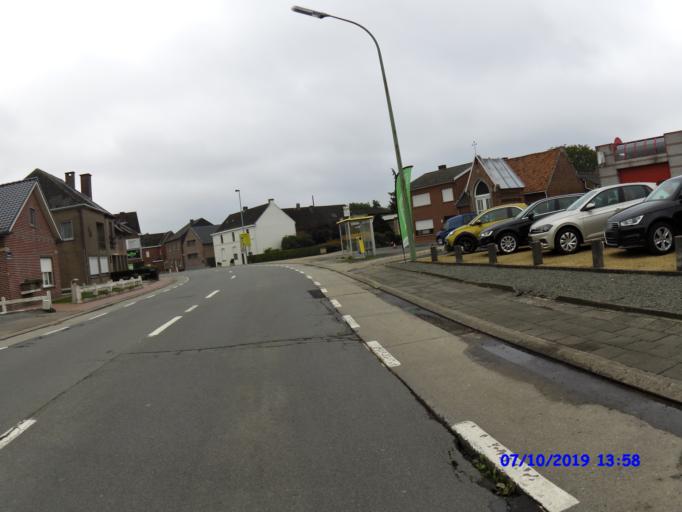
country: BE
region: Flanders
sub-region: Provincie Oost-Vlaanderen
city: Zottegem
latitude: 50.8949
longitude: 3.8064
